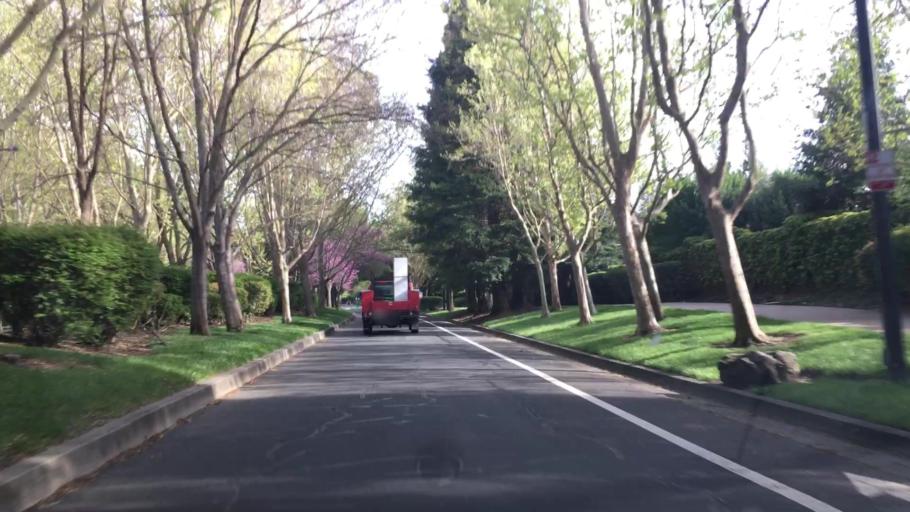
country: US
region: California
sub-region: Solano County
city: Green Valley
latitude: 38.2282
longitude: -122.1484
